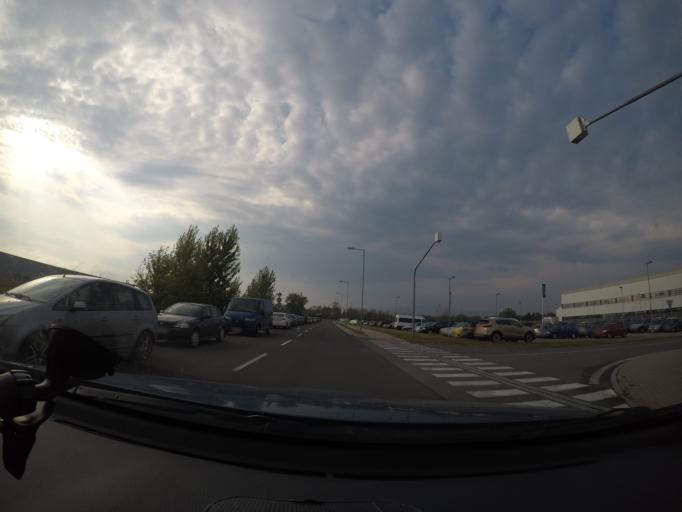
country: SK
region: Trenciansky
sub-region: Okres Trencin
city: Trencin
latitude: 48.8882
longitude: 17.9992
